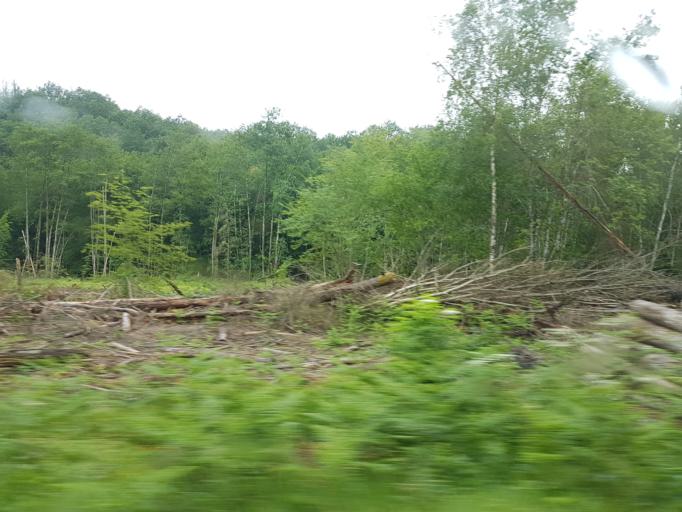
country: FR
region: Bourgogne
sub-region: Departement de la Nievre
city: Corbigny
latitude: 47.1803
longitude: 3.7571
